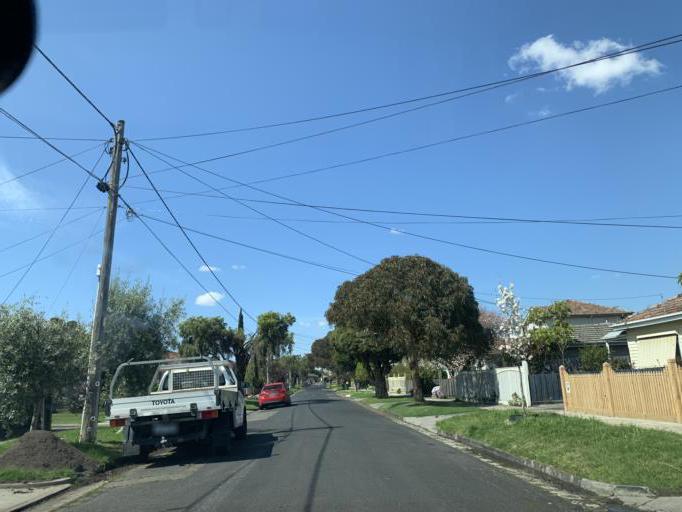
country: AU
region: Victoria
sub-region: Moreland
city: Pascoe Vale South
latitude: -37.7332
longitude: 144.9472
